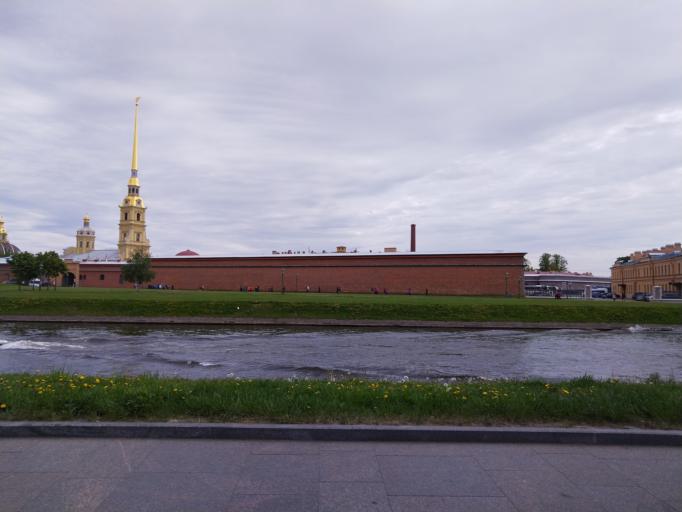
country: RU
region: St.-Petersburg
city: Saint Petersburg
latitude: 59.9509
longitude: 30.3101
